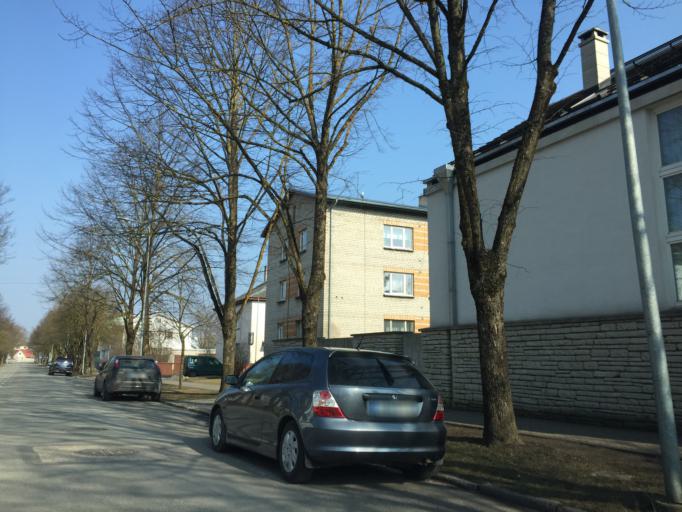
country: EE
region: Saare
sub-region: Kuressaare linn
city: Kuressaare
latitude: 58.2553
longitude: 22.4858
